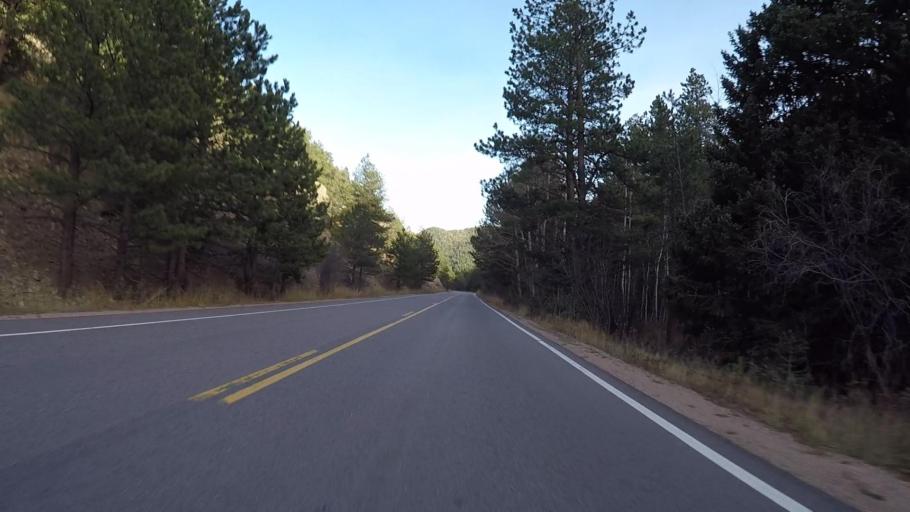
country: US
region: Colorado
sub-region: Boulder County
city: Nederland
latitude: 40.0626
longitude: -105.4764
